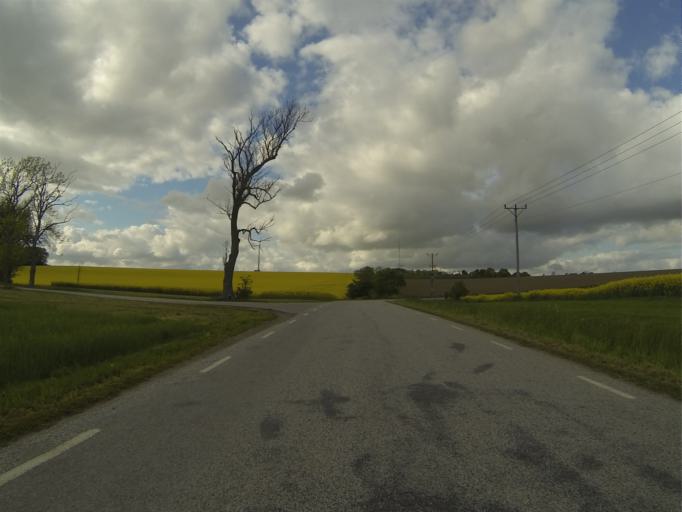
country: SE
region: Skane
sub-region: Staffanstorps Kommun
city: Staffanstorp
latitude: 55.6912
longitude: 13.2871
